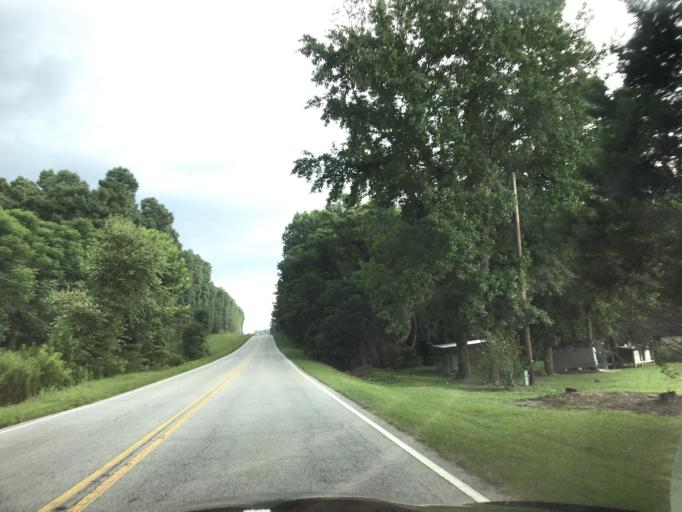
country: US
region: North Carolina
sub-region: Johnston County
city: Four Oaks
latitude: 35.5147
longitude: -78.4935
